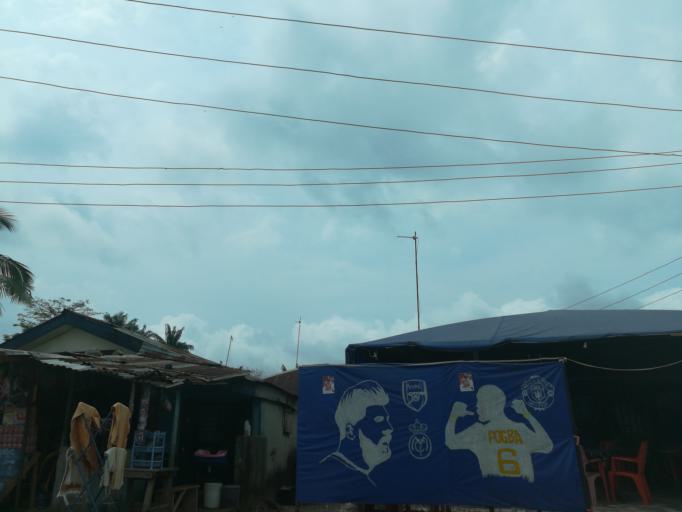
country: NG
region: Rivers
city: Port Harcourt
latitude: 4.9032
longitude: 6.9900
